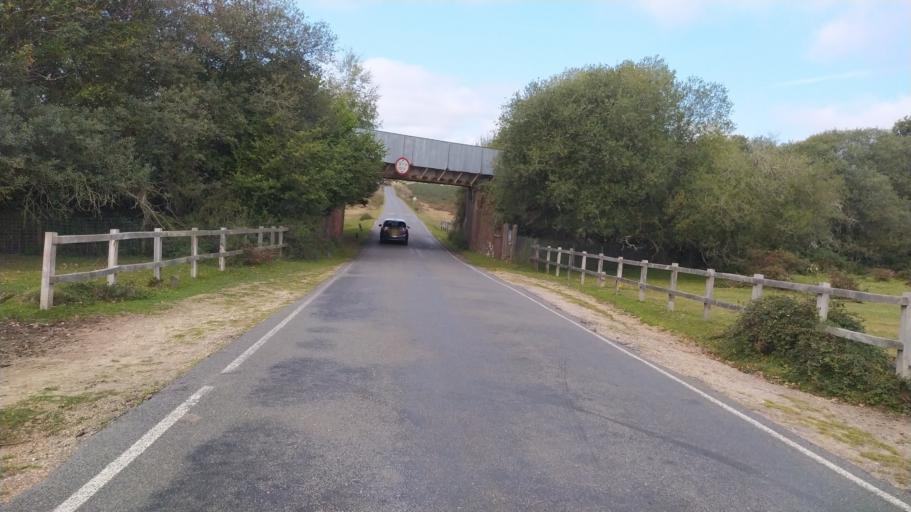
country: GB
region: England
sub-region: Hampshire
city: Sway
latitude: 50.7942
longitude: -1.5806
